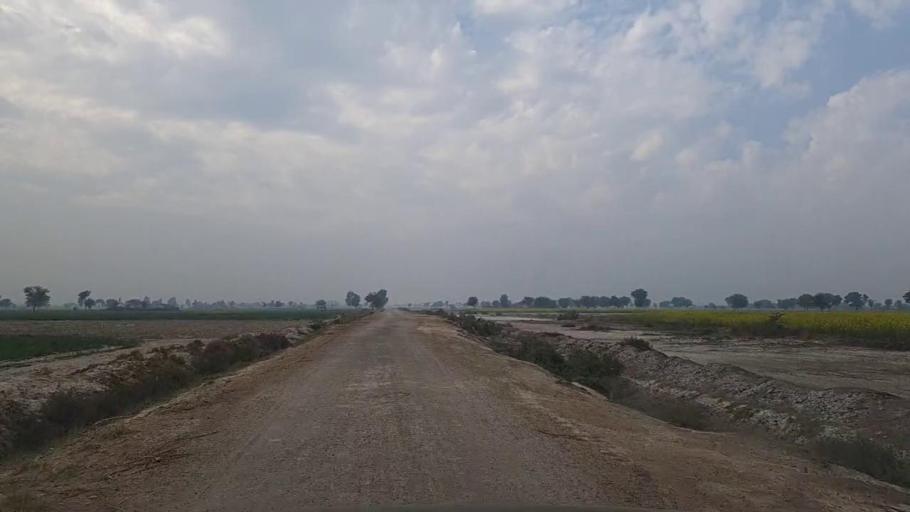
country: PK
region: Sindh
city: Nawabshah
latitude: 26.3652
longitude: 68.3987
